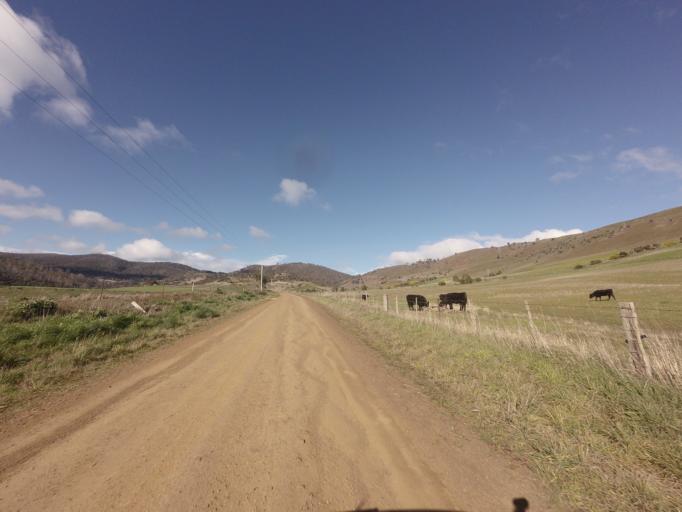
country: AU
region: Tasmania
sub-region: Derwent Valley
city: New Norfolk
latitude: -42.6995
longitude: 146.9815
